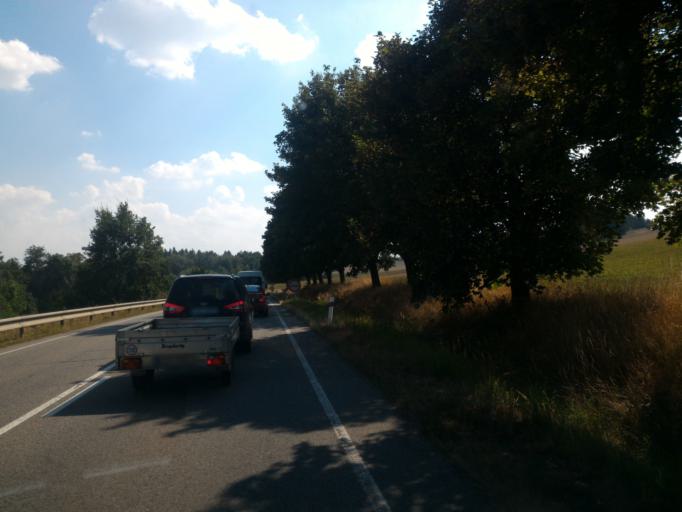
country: CZ
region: Vysocina
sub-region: Okres Jihlava
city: Trest'
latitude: 49.3127
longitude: 15.4808
